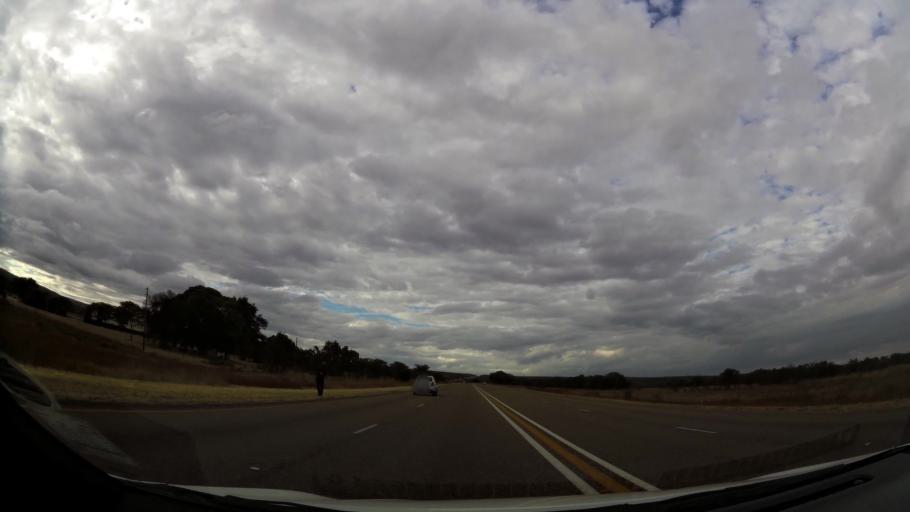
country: ZA
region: Limpopo
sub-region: Waterberg District Municipality
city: Modimolle
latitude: -24.6492
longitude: 28.5905
